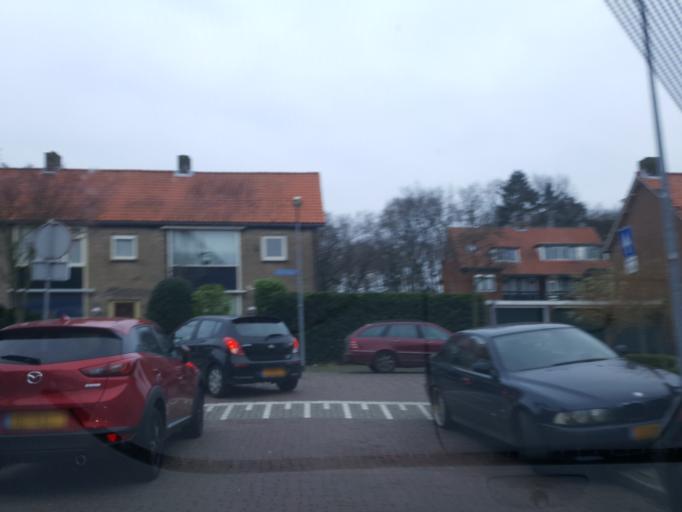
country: NL
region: North Holland
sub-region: Gemeente Wijdemeren
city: Nieuw-Loosdrecht
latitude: 52.2174
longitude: 5.1501
